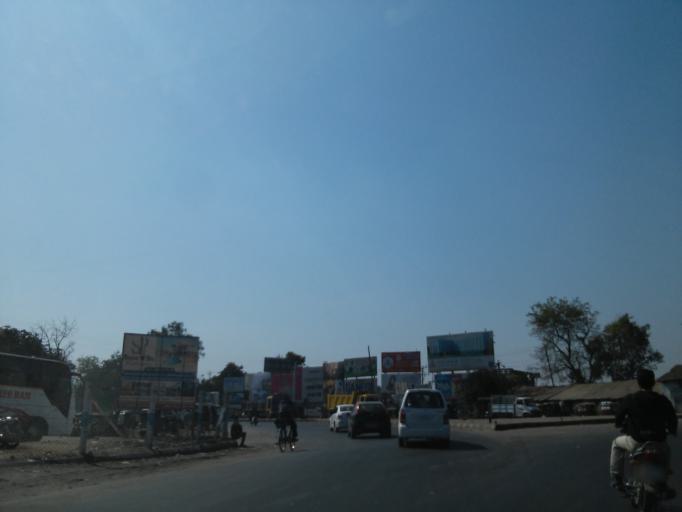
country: IN
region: Gujarat
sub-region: Gandhinagar
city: Ghandinagar
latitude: 23.2267
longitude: 72.7311
